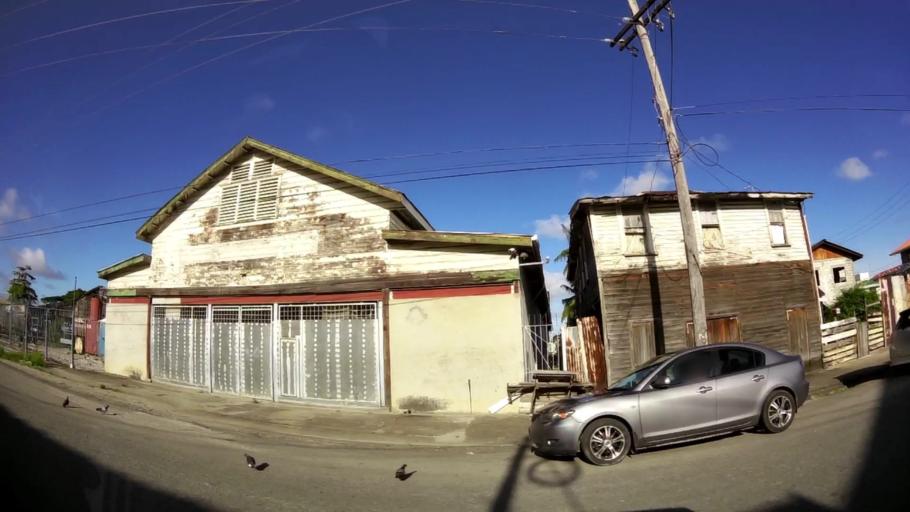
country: GY
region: Demerara-Mahaica
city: Georgetown
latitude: 6.8193
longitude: -58.1657
